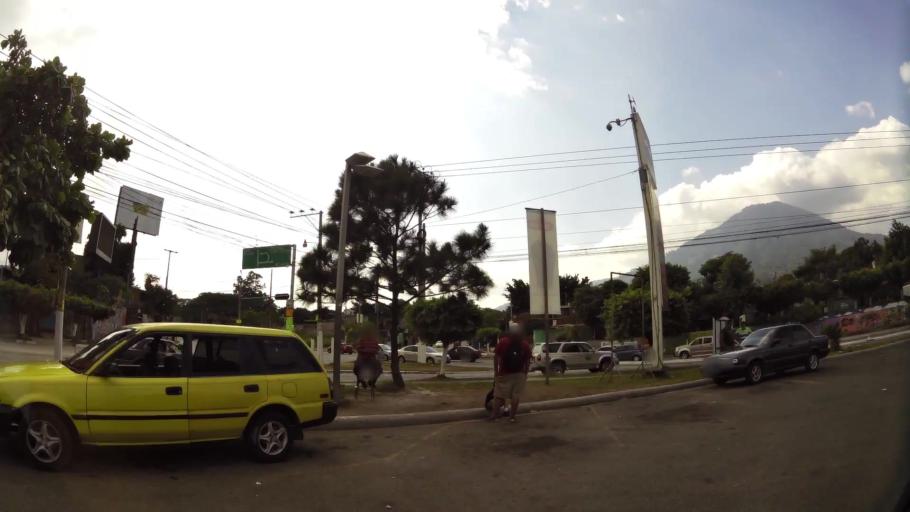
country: SV
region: San Salvador
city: Mejicanos
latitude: 13.7348
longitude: -89.2176
